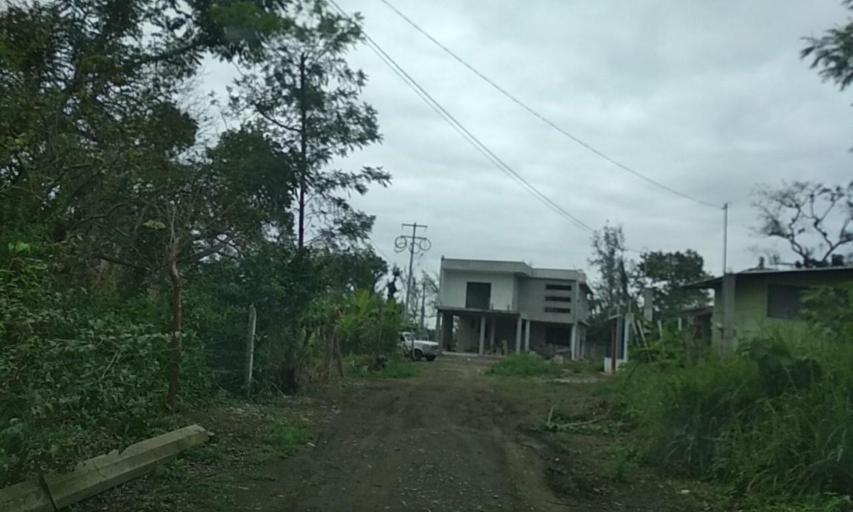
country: MX
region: Veracruz
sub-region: Papantla
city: Residencial Tajin
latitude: 20.5980
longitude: -97.4206
